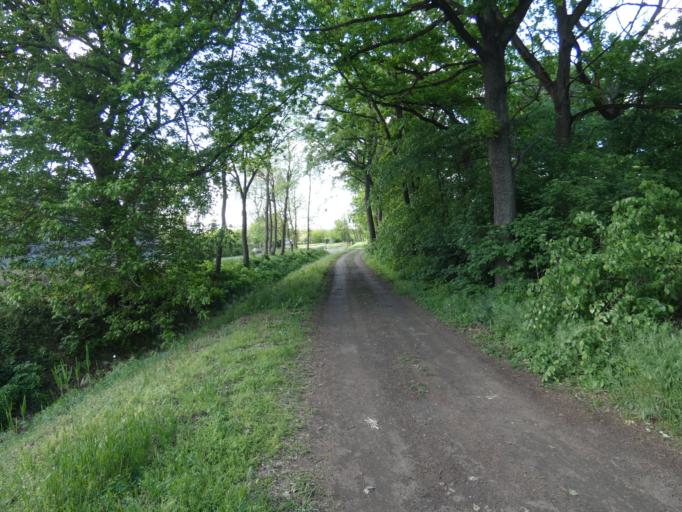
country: HU
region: Szabolcs-Szatmar-Bereg
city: Kotaj
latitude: 48.0084
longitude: 21.7211
